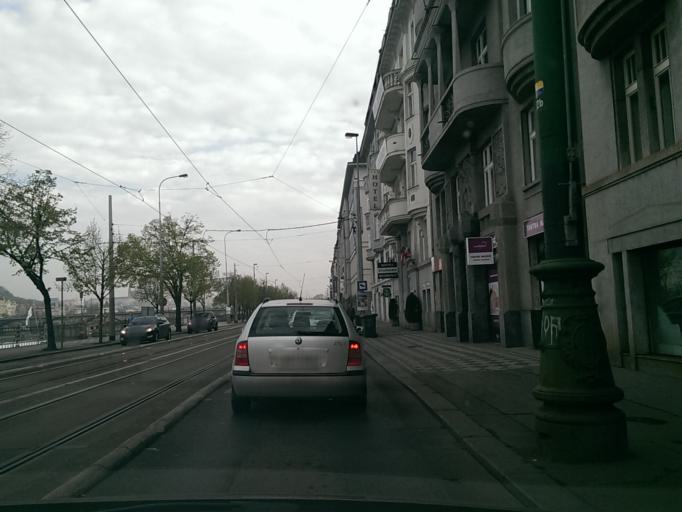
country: CZ
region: Praha
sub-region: Praha 2
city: Vysehrad
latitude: 50.0685
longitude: 14.4149
